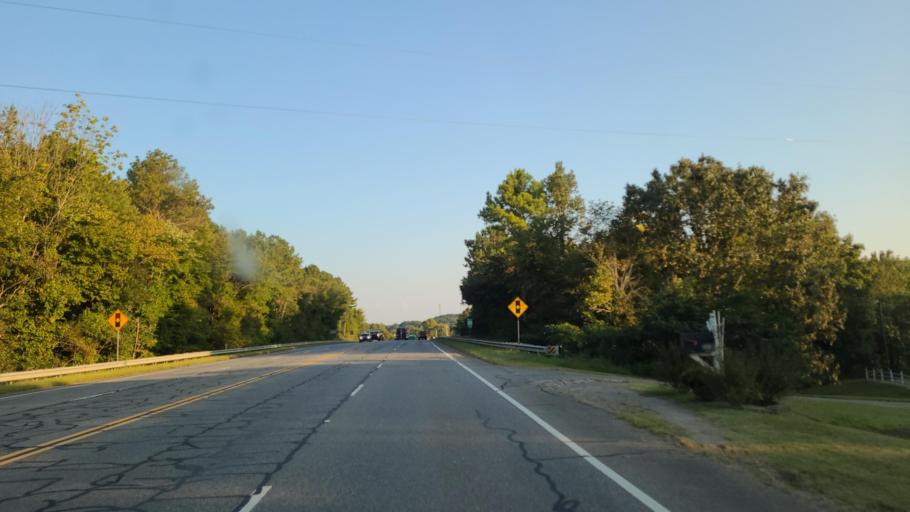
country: US
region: Georgia
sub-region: Murray County
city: Chatsworth
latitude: 34.7013
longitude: -84.7410
